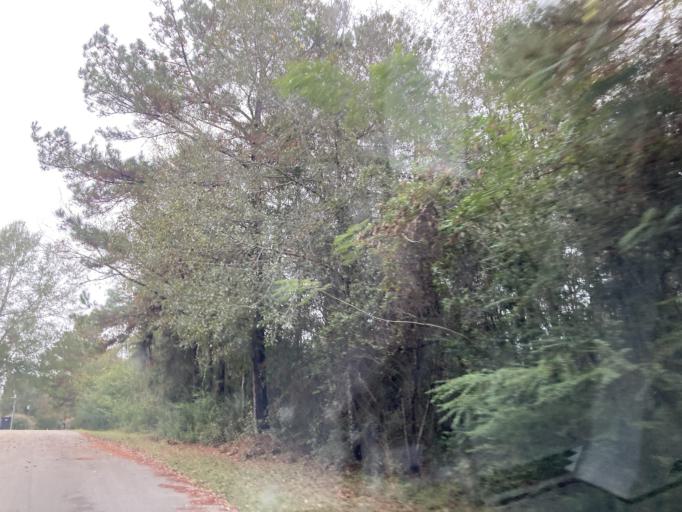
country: US
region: Mississippi
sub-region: Lamar County
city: Purvis
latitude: 31.1846
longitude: -89.4106
